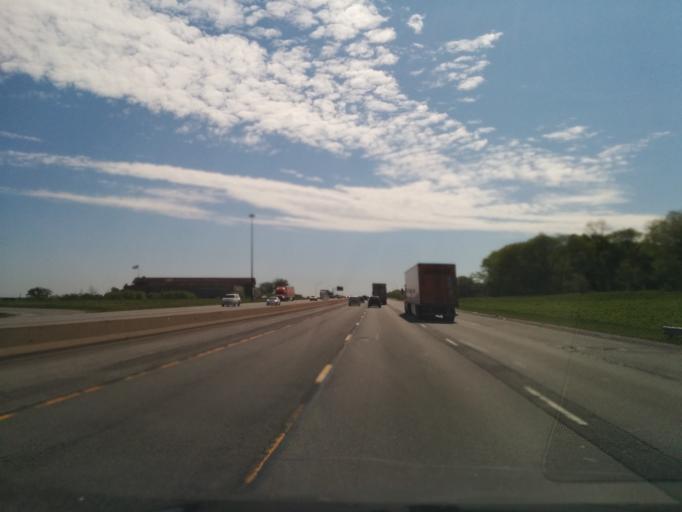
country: US
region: Indiana
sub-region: Porter County
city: Portage
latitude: 41.6019
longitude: -87.1736
